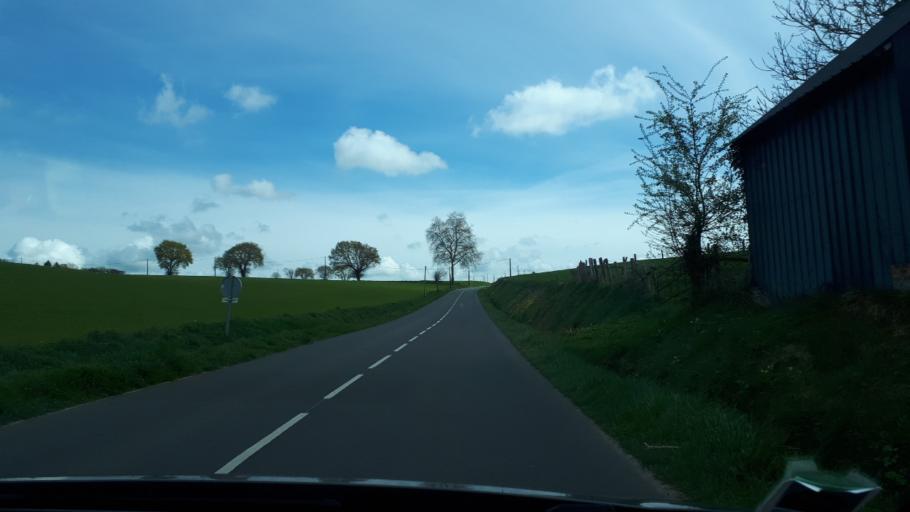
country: FR
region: Pays de la Loire
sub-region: Departement de la Sarthe
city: Le Grand-Luce
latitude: 47.8675
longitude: 0.4871
